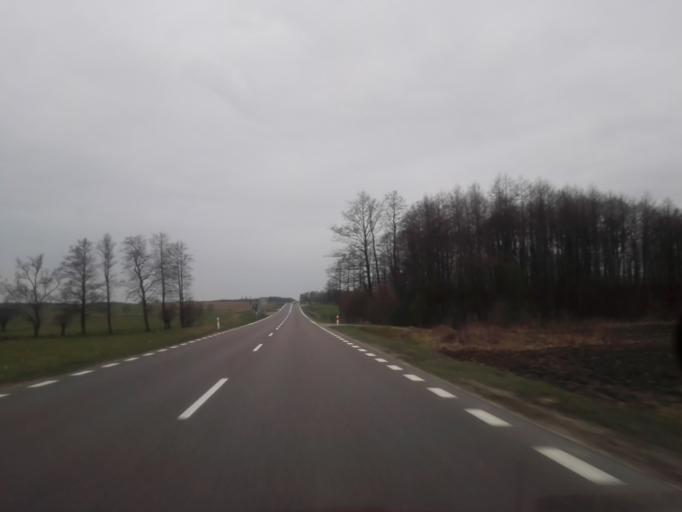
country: PL
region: Podlasie
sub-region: Powiat grajewski
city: Szczuczyn
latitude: 53.5348
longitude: 22.2613
